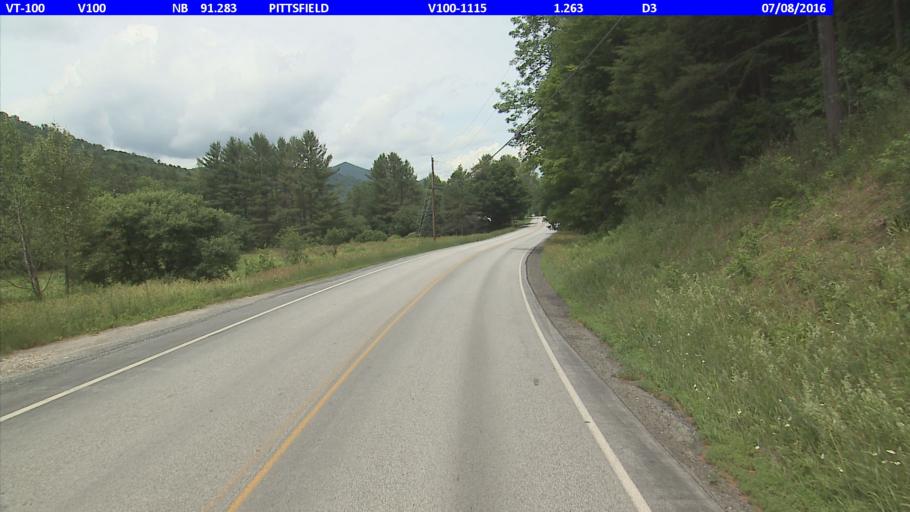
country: US
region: Vermont
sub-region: Rutland County
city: Rutland
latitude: 43.7353
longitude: -72.8208
